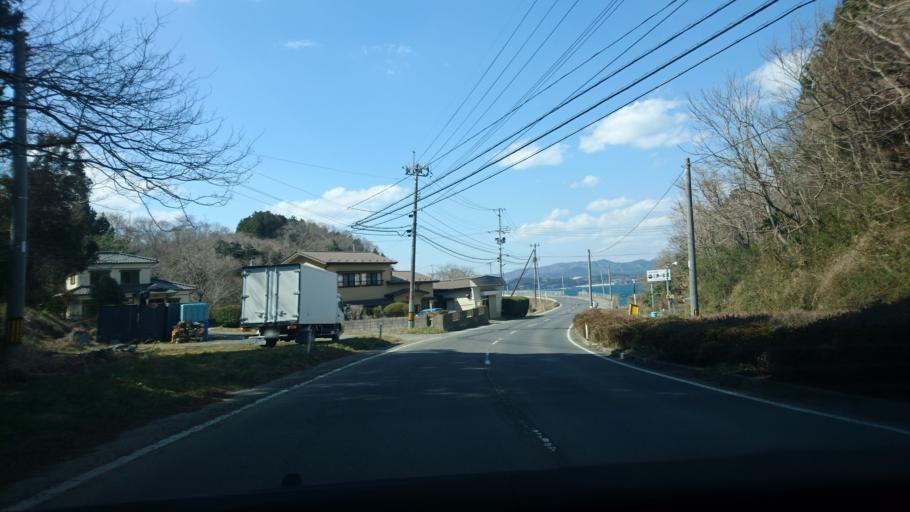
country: JP
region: Miyagi
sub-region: Oshika Gun
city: Onagawa Cho
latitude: 38.6417
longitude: 141.4812
